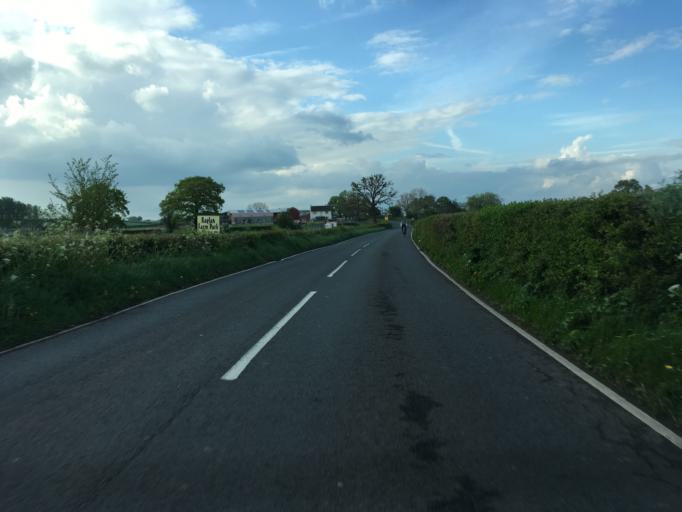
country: GB
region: Wales
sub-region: Monmouthshire
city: Llangwm
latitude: 51.7523
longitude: -2.8465
